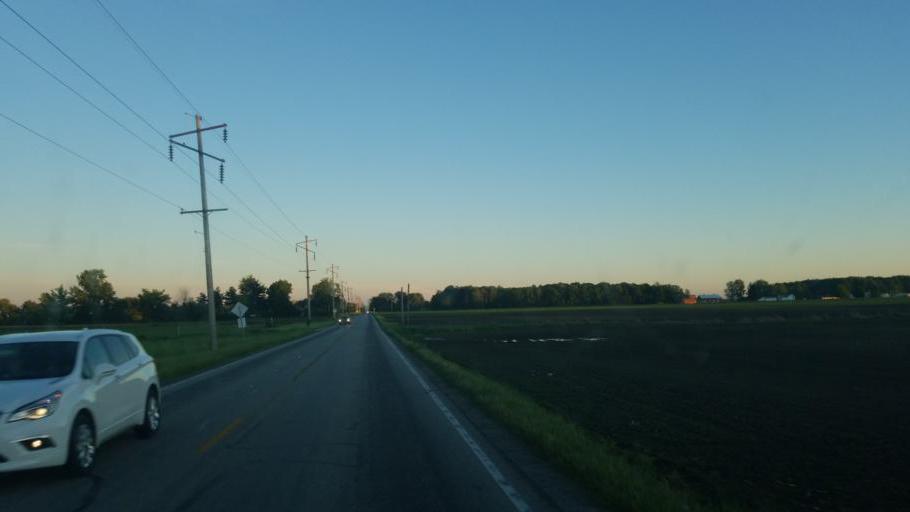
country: US
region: Indiana
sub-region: Elkhart County
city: Nappanee
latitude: 41.3964
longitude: -86.0010
